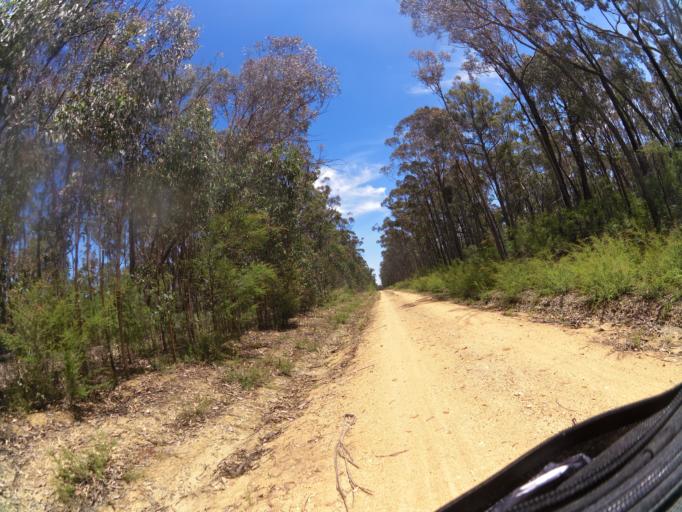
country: AU
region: Victoria
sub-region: East Gippsland
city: Lakes Entrance
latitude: -37.7566
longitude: 147.9650
